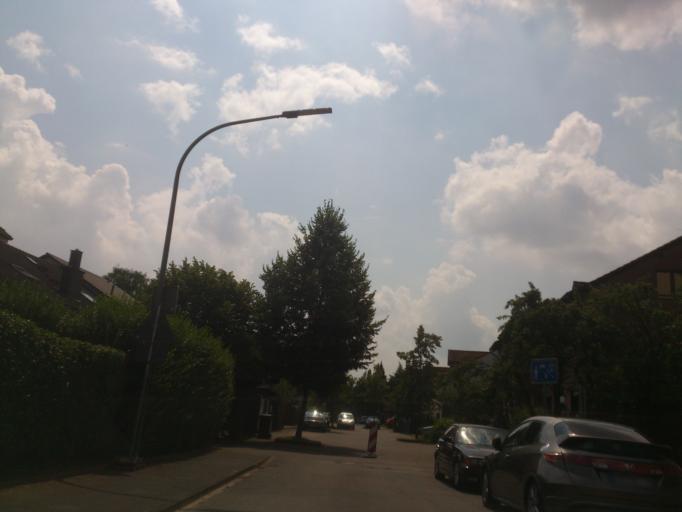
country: DE
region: North Rhine-Westphalia
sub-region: Regierungsbezirk Detmold
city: Paderborn
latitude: 51.7132
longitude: 8.7254
